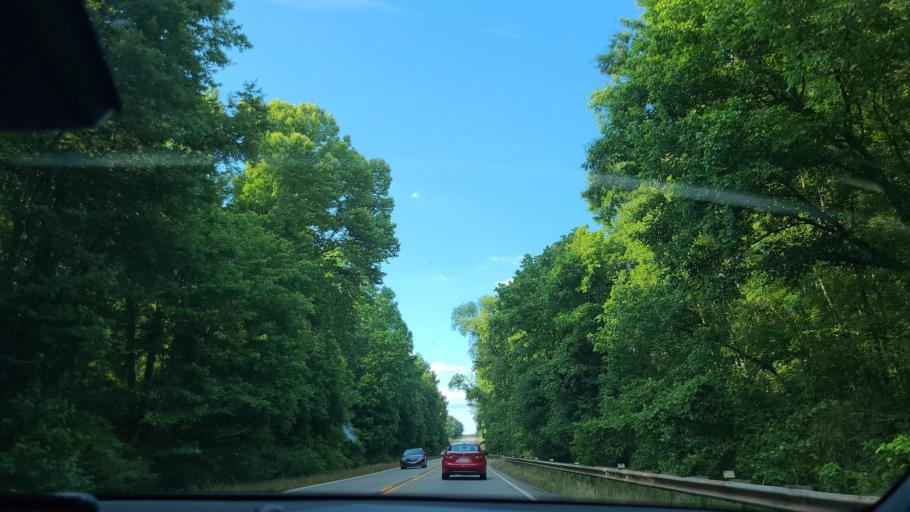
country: US
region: Georgia
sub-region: Morgan County
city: Madison
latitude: 33.6728
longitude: -83.4438
